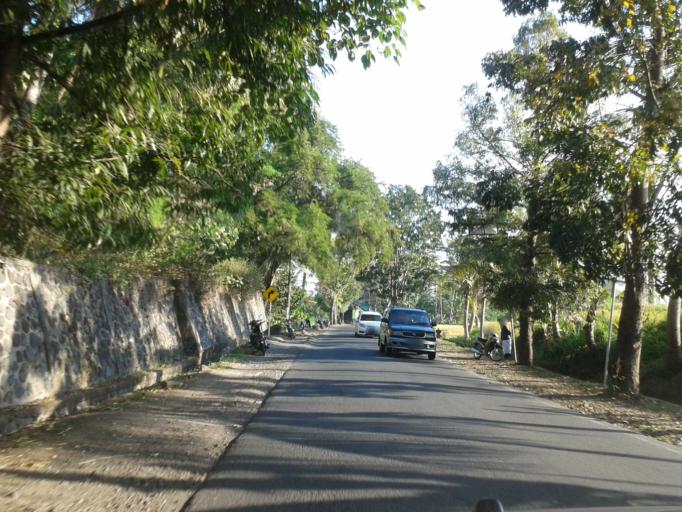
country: ID
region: Bali
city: Banjar Wangsian
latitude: -8.5016
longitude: 115.4040
